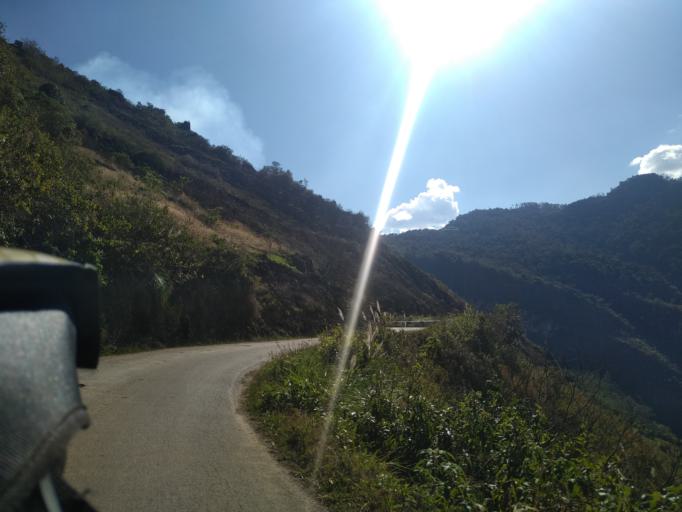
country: PE
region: Amazonas
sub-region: Provincia de Chachapoyas
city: Montevideo
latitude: -6.7137
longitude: -77.8155
